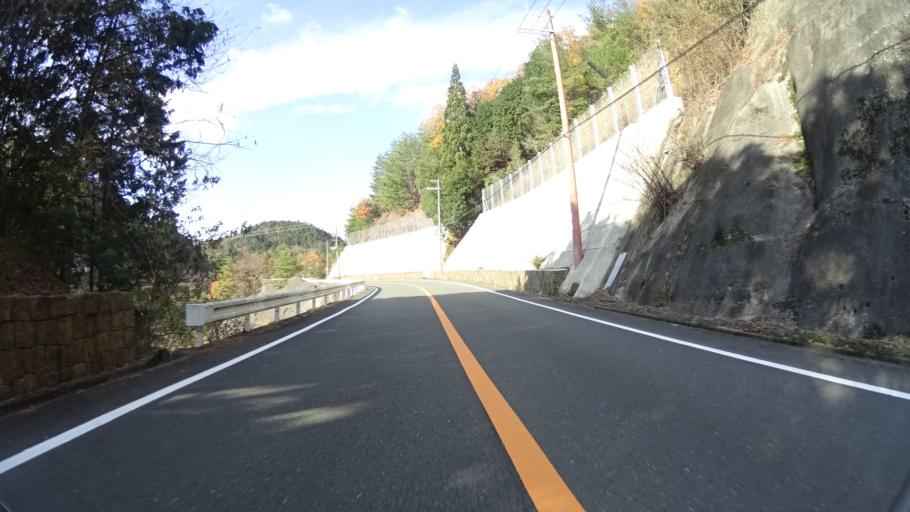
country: JP
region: Kyoto
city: Kameoka
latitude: 35.1326
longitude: 135.5382
